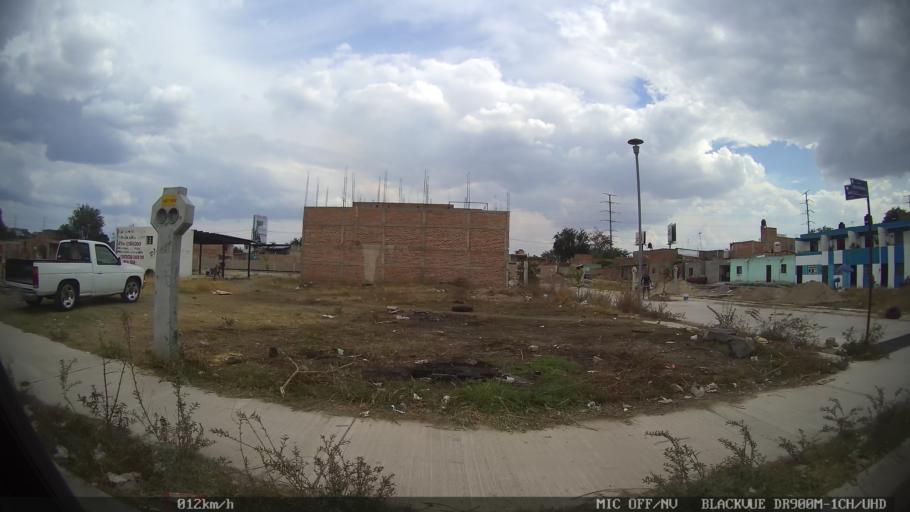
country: MX
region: Jalisco
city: Tlaquepaque
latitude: 20.6228
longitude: -103.2734
